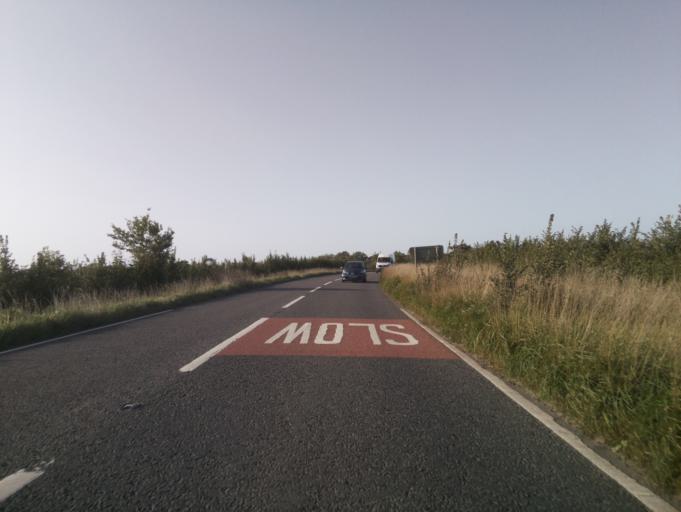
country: GB
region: England
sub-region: Gloucestershire
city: Gloucester
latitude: 51.9425
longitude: -2.2982
